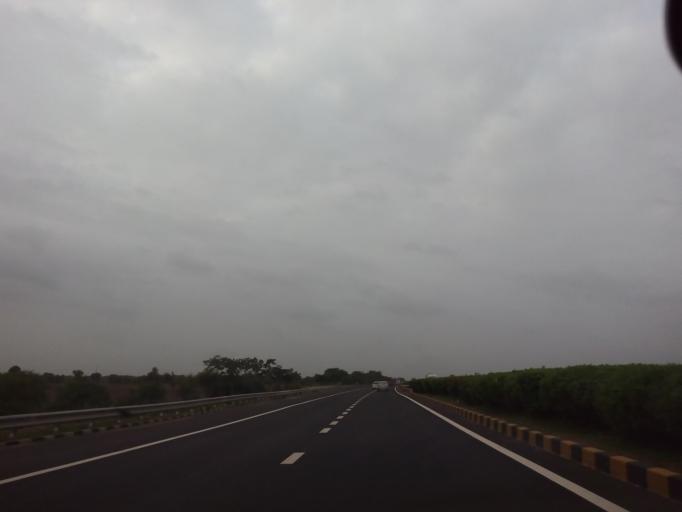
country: IN
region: Gujarat
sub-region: Kheda
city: Nadiad
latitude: 22.7492
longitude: 72.8606
